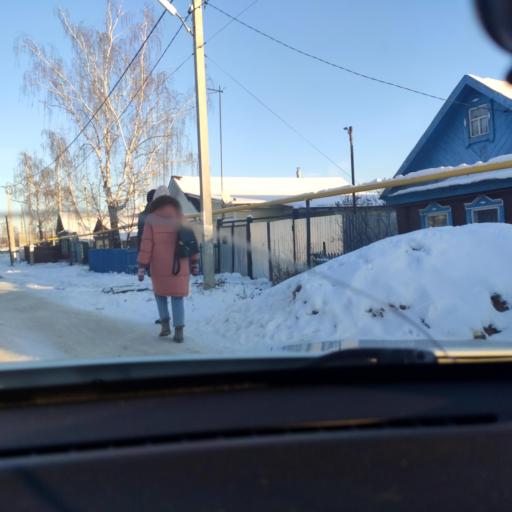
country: RU
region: Tatarstan
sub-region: Gorod Kazan'
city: Kazan
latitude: 55.7298
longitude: 49.1415
